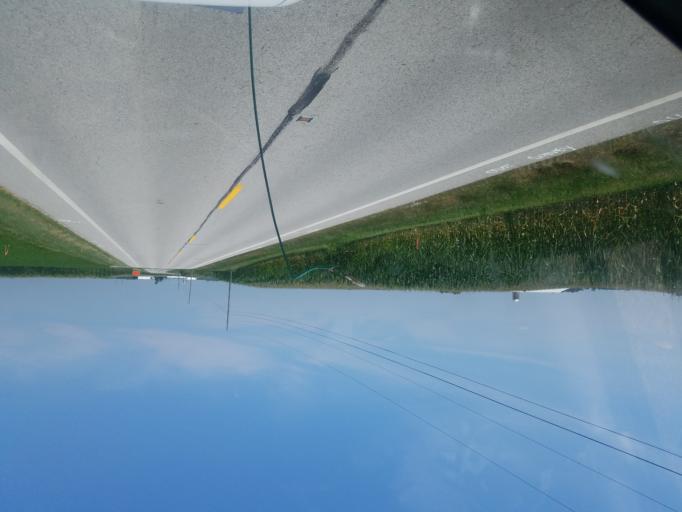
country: US
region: Ohio
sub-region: Auglaize County
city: New Bremen
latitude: 40.4614
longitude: -84.4341
